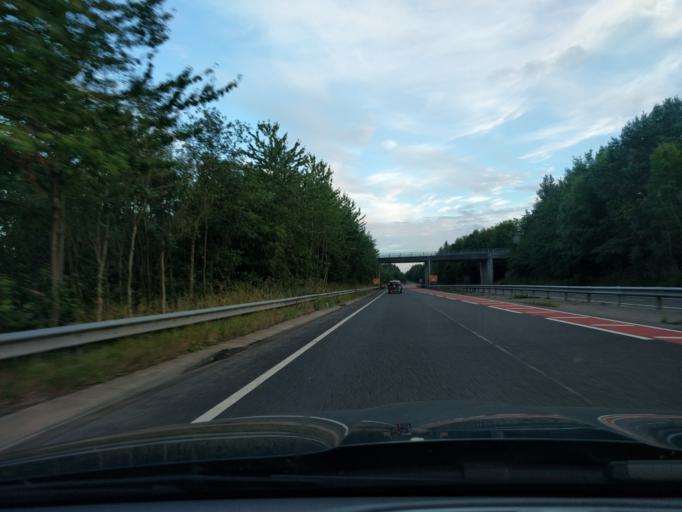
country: GB
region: England
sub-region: Northumberland
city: Felton
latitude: 55.3023
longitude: -1.7260
